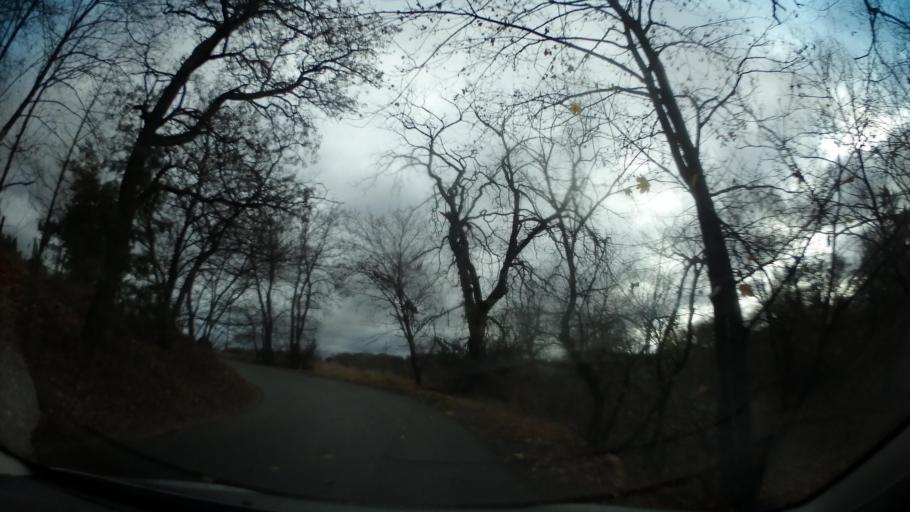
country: CZ
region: Vysocina
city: Namest' nad Oslavou
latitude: 49.2851
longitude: 16.1056
